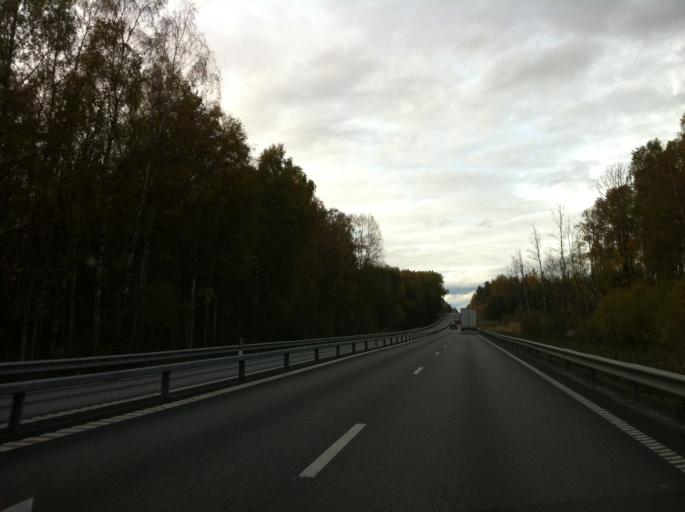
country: SE
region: OErebro
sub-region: Askersunds Kommun
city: Askersund
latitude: 58.7862
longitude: 14.9907
